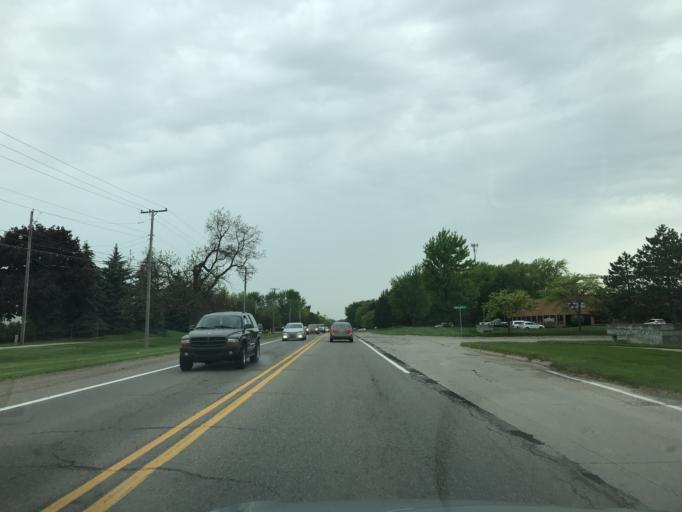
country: US
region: Michigan
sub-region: Oakland County
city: Wixom
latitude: 42.4966
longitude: -83.5462
